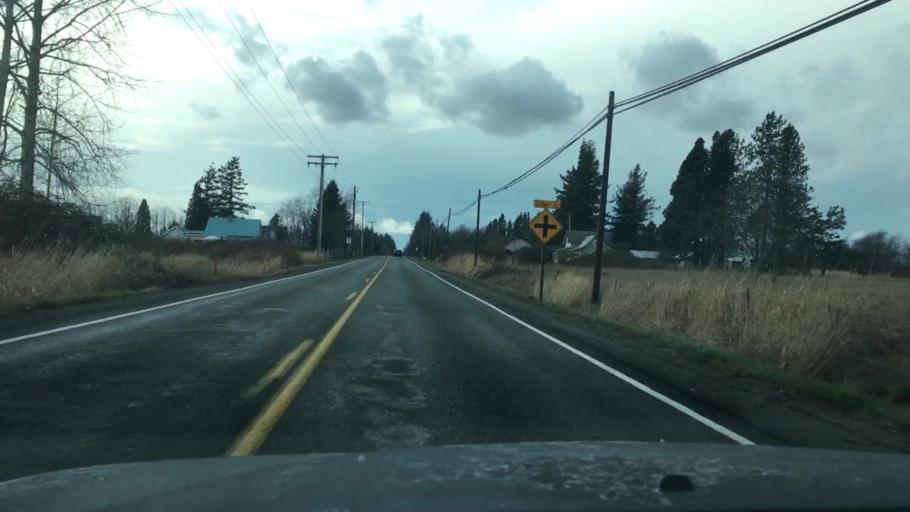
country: US
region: Washington
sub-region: Whatcom County
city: Ferndale
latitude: 48.8483
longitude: -122.6582
